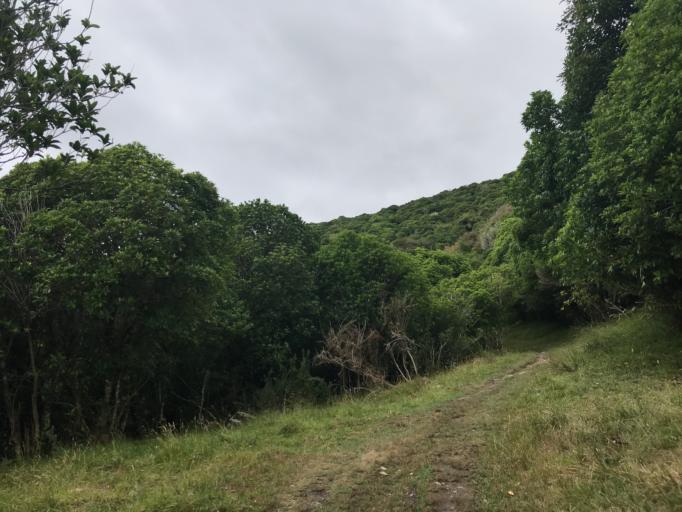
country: NZ
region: Marlborough
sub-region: Marlborough District
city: Picton
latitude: -41.2336
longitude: 173.9582
